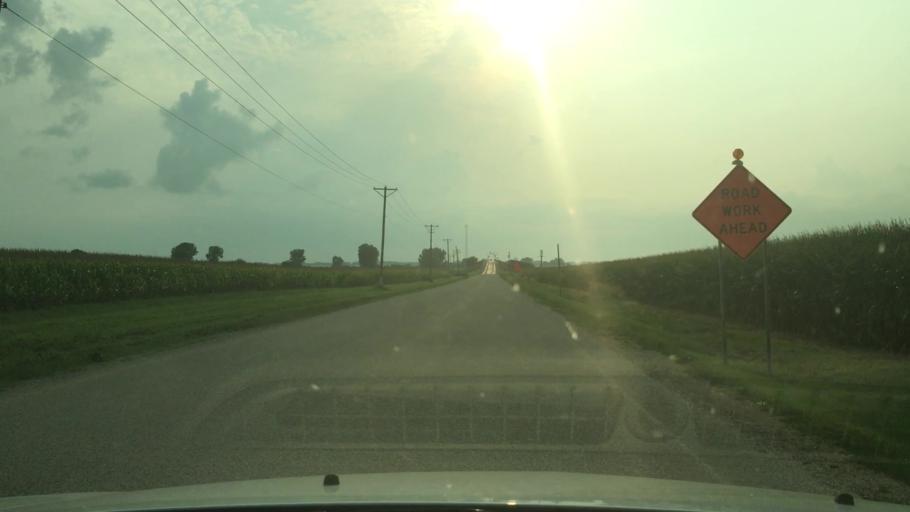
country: US
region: Illinois
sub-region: Ogle County
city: Rochelle
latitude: 41.9201
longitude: -89.0157
